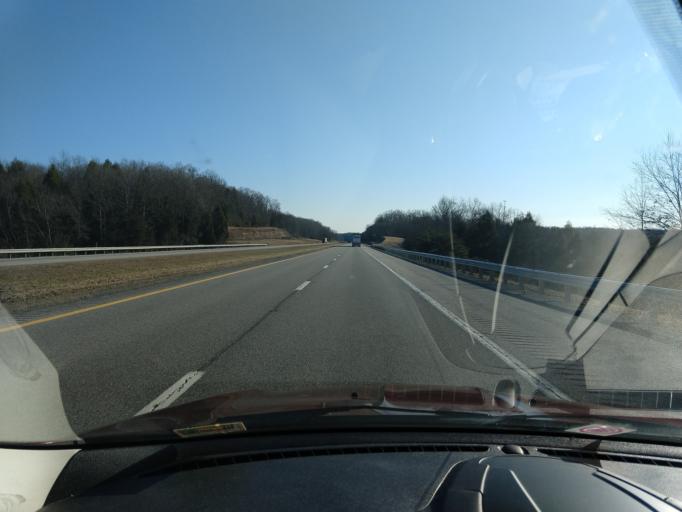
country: US
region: West Virginia
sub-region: Fayette County
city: Ansted
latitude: 38.1325
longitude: -80.9478
